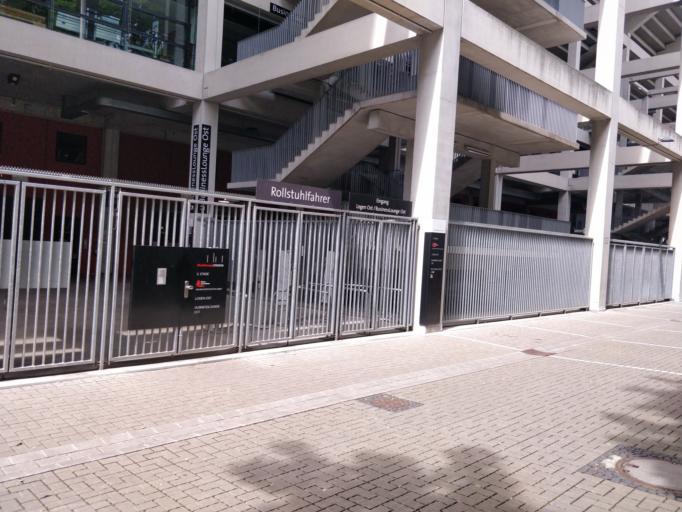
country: DE
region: North Rhine-Westphalia
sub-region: Regierungsbezirk Koln
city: Mengenich
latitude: 50.9333
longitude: 6.8764
